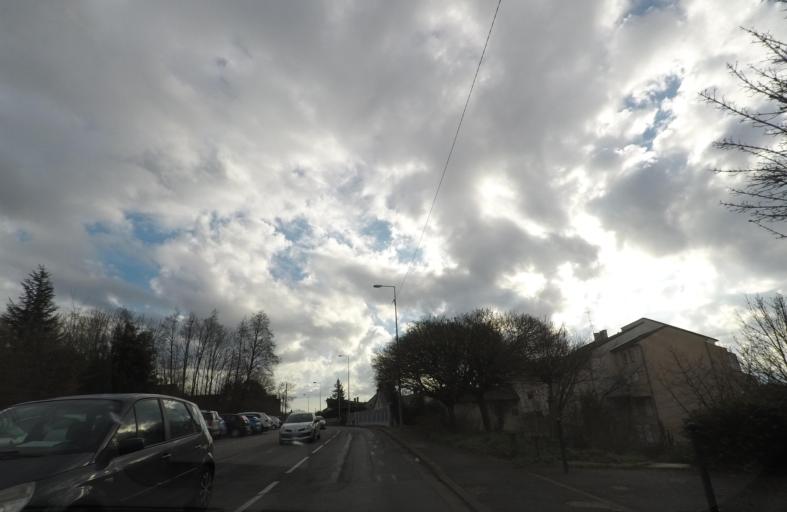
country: FR
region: Centre
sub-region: Departement du Cher
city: Bourges
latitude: 47.0601
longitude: 2.4016
